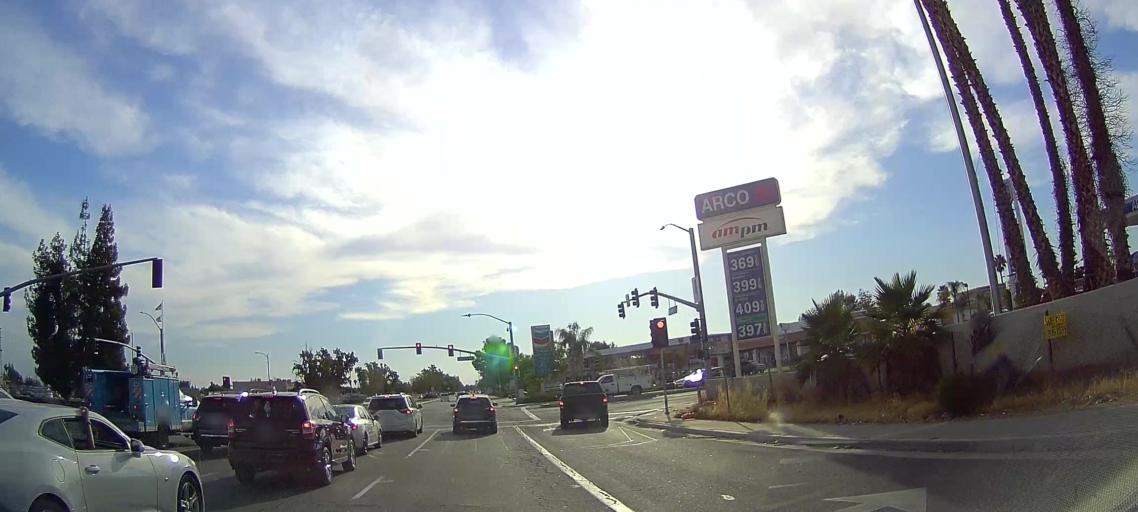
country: US
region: California
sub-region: Kern County
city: Bakersfield
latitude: 35.3178
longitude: -119.0384
